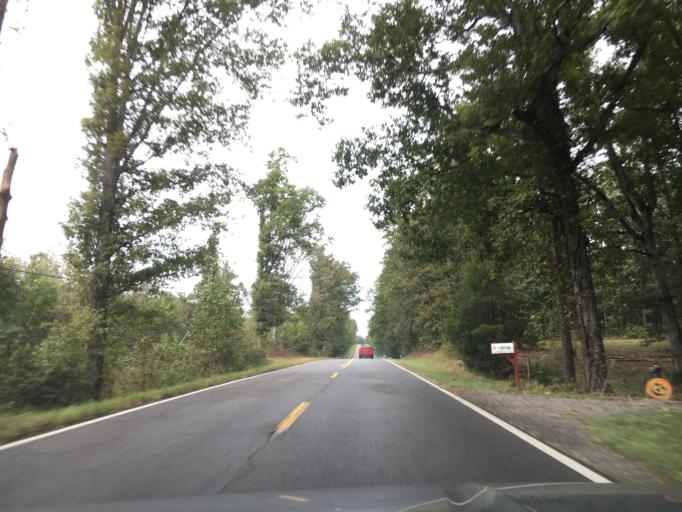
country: US
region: Virginia
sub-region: Goochland County
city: Goochland
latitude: 37.7561
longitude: -77.8680
